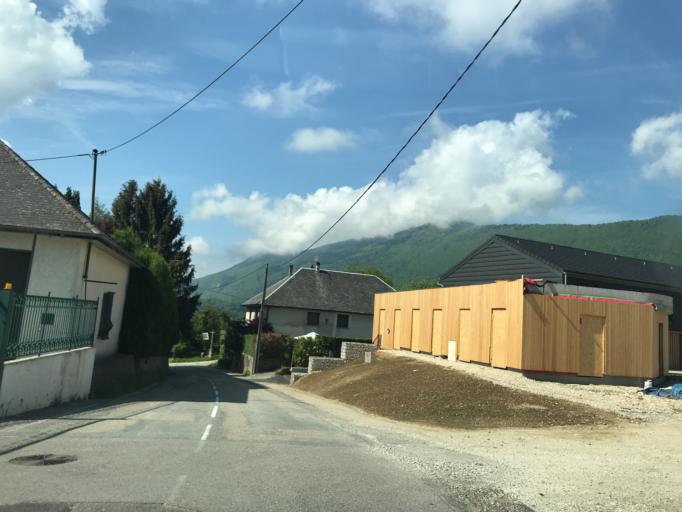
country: FR
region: Rhone-Alpes
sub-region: Departement de la Savoie
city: Vimines
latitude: 45.5455
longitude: 5.8650
